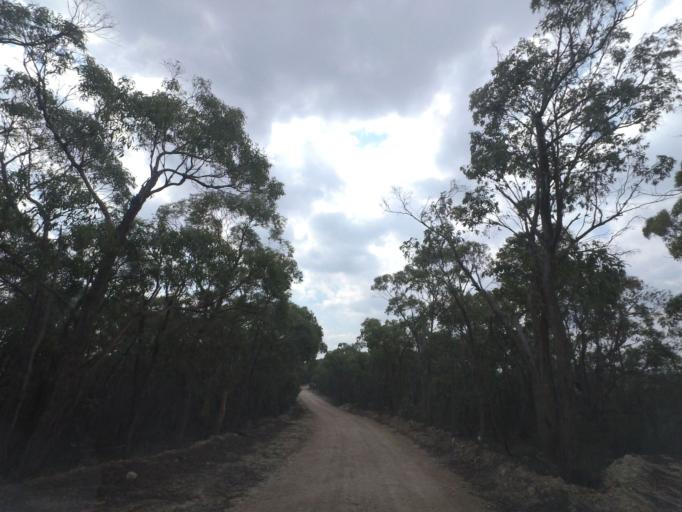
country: AU
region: Victoria
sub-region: Moorabool
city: Bacchus Marsh
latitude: -37.5543
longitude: 144.4219
